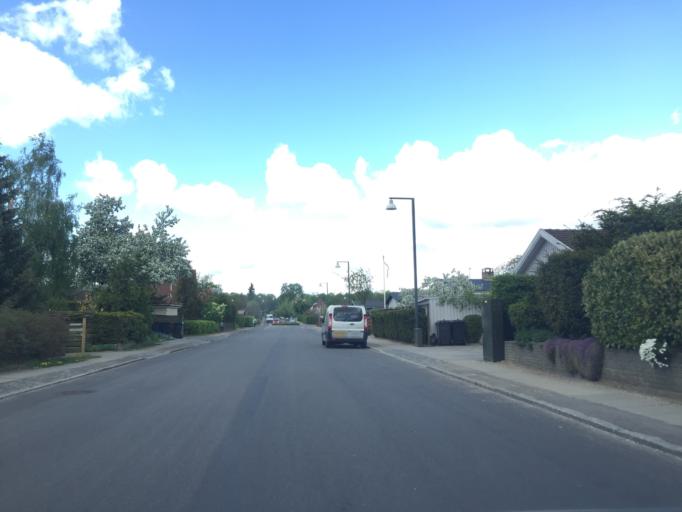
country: DK
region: Capital Region
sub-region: Rodovre Kommune
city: Rodovre
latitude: 55.6857
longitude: 12.4432
